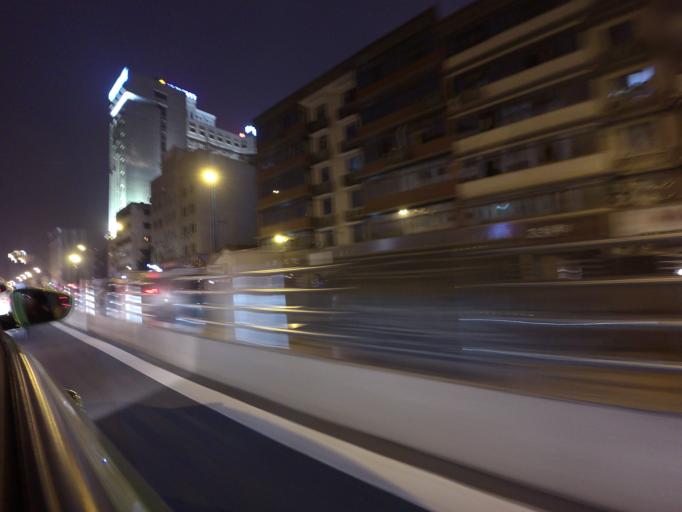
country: CN
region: Sichuan
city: Chengdu
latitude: 30.6577
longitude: 104.0583
